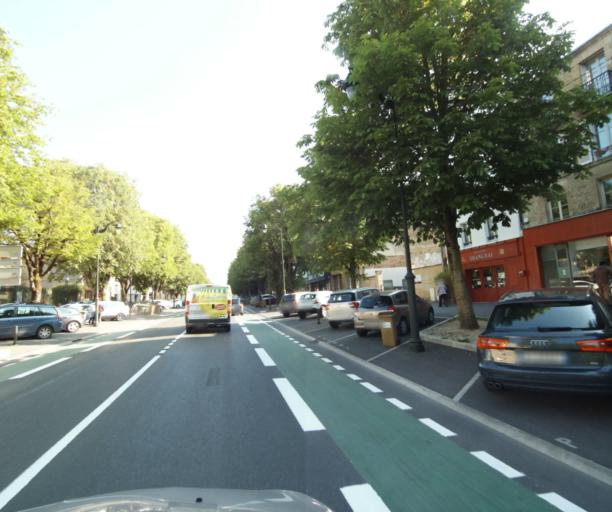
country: FR
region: Champagne-Ardenne
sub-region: Departement des Ardennes
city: Charleville-Mezieres
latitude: 49.7683
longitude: 4.7195
